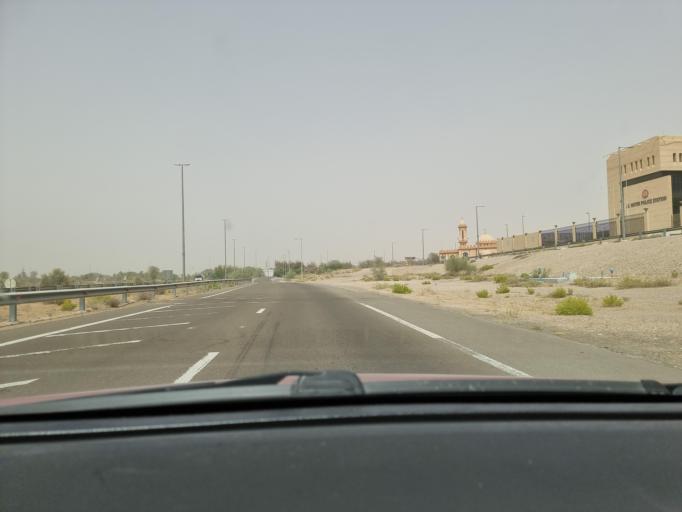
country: OM
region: Al Buraimi
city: Al Buraymi
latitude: 24.5822
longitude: 55.7360
